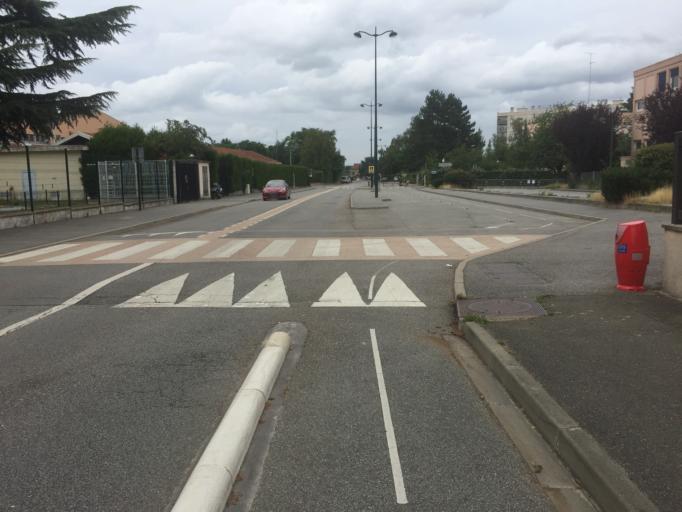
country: FR
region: Ile-de-France
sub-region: Departement des Yvelines
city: Les Clayes-sous-Bois
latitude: 48.8268
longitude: 1.9821
